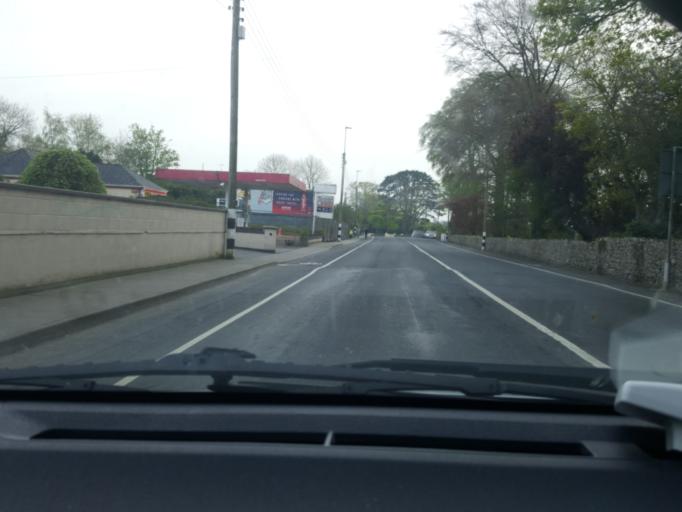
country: IE
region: Munster
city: Cahir
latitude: 52.3818
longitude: -7.9199
